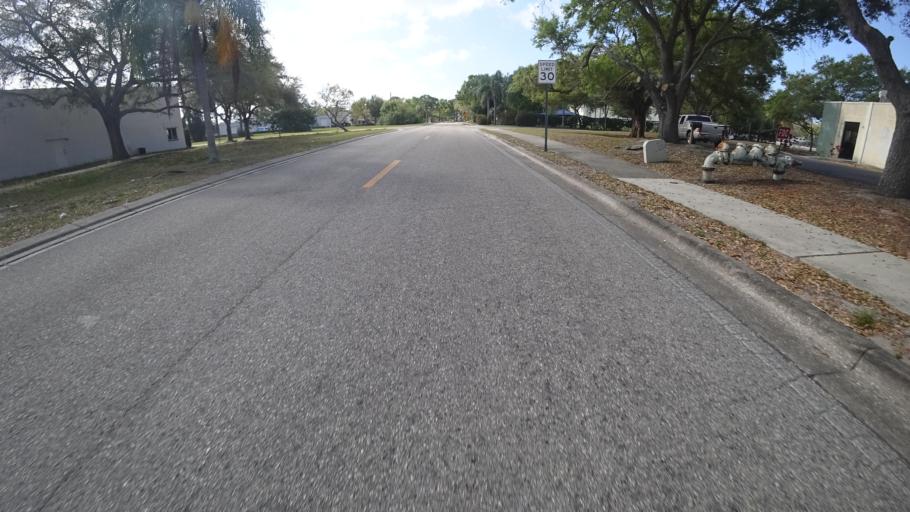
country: US
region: Florida
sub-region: Manatee County
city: Whitfield
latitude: 27.4086
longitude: -82.5551
